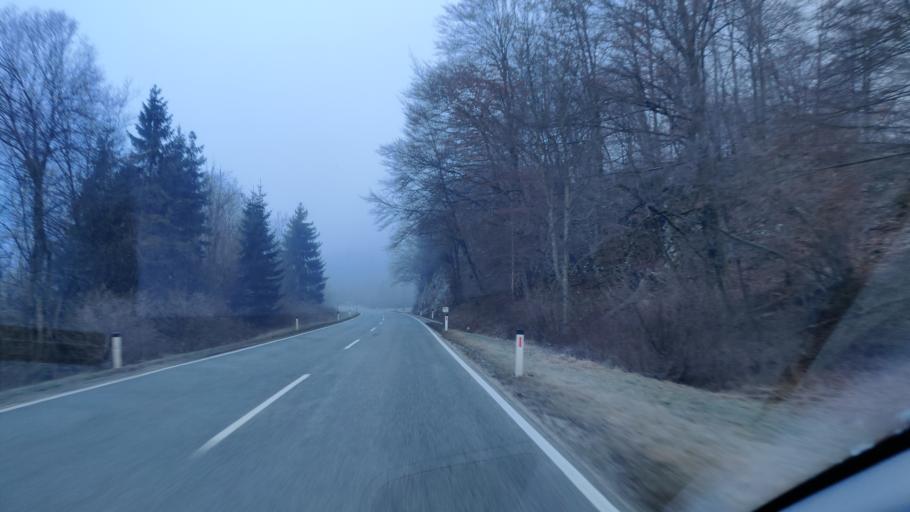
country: SI
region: Bohinj
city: Bohinjska Bistrica
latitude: 46.2882
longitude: 13.9846
